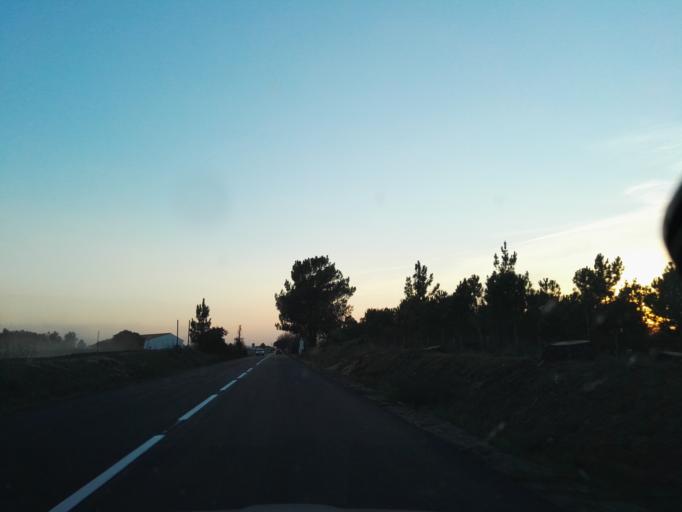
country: PT
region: Santarem
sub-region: Coruche
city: Coruche
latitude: 38.9642
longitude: -8.4845
